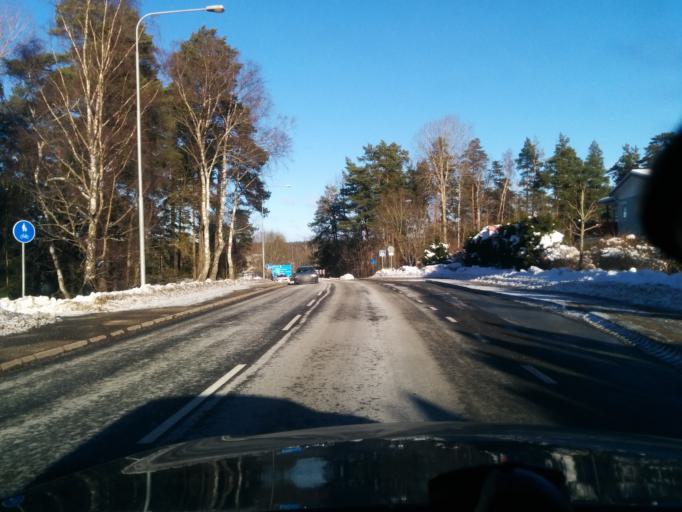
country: SE
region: Stockholm
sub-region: Taby Kommun
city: Taby
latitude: 59.4690
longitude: 18.0941
